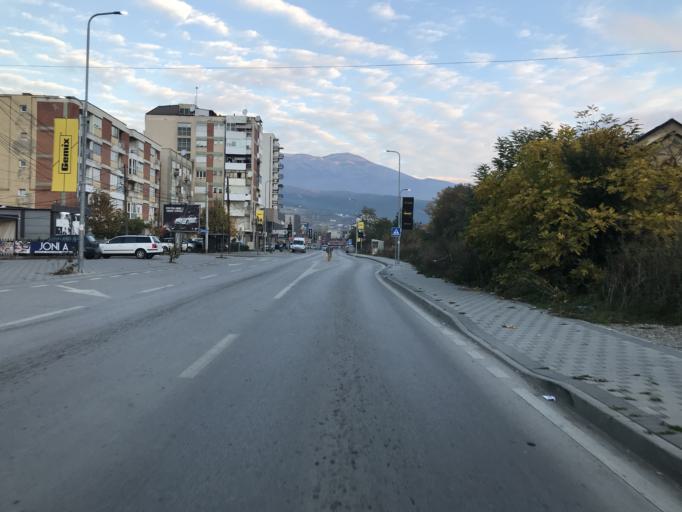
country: XK
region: Pec
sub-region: Komuna e Pejes
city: Peje
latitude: 42.6580
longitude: 20.3056
